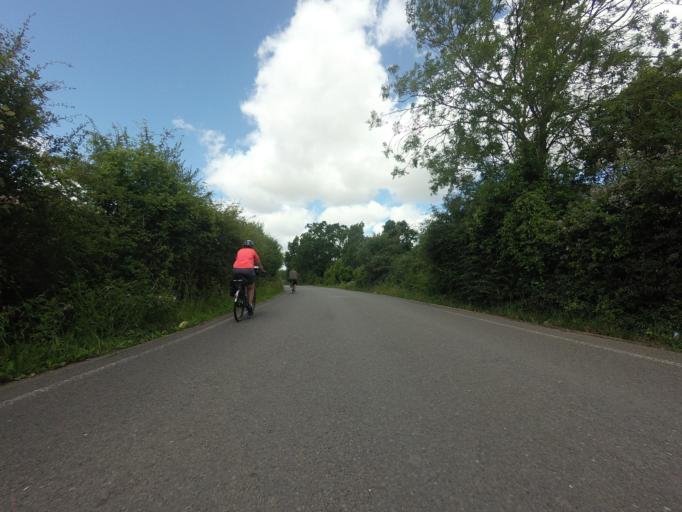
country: GB
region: England
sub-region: Kent
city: Cliffe
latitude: 51.4362
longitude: 0.4592
